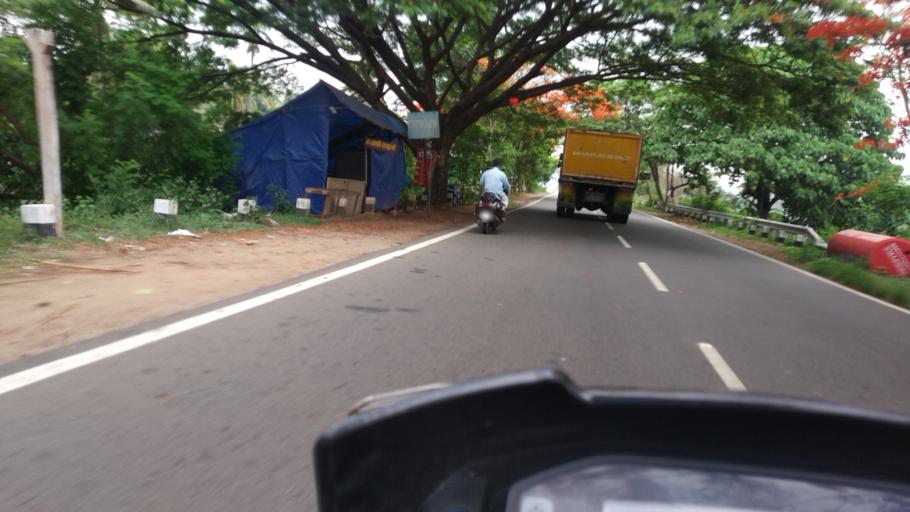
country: IN
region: Kerala
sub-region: Ernakulam
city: Elur
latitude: 10.1508
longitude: 76.2694
